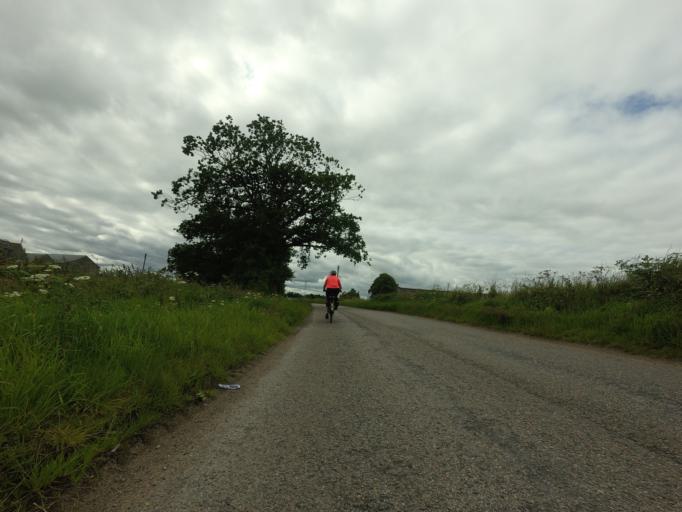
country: GB
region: Scotland
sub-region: Moray
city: Forres
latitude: 57.6223
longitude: -3.6134
